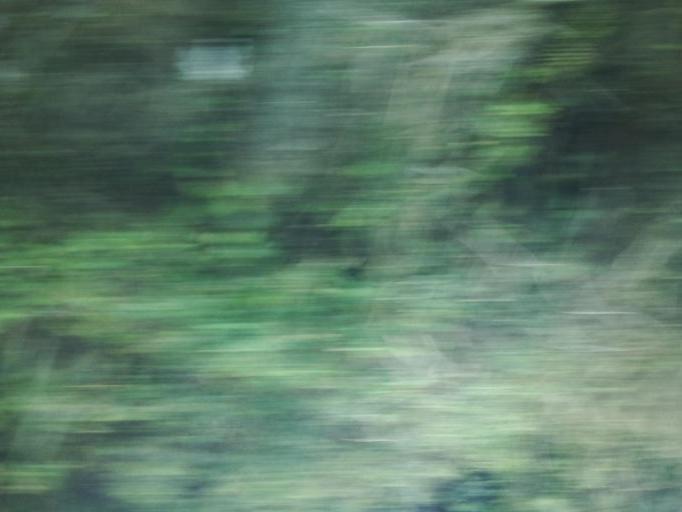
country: BR
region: Minas Gerais
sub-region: Ipaba
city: Ipaba
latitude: -19.4635
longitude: -42.4562
